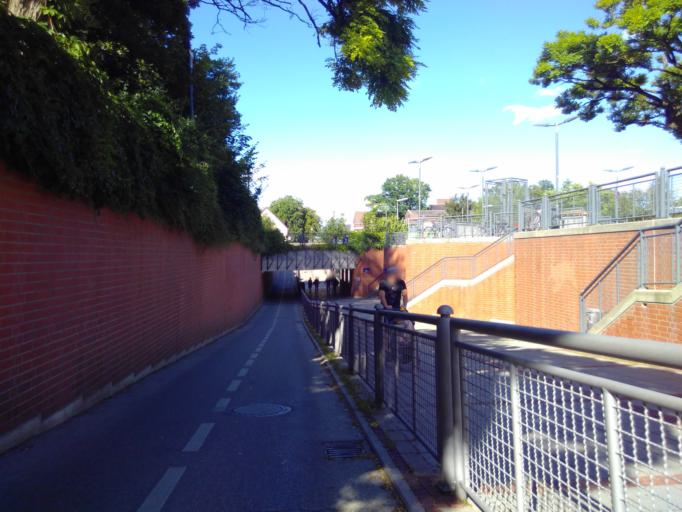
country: DE
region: Bavaria
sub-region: Upper Bavaria
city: Puchheim
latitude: 48.1721
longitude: 11.3516
